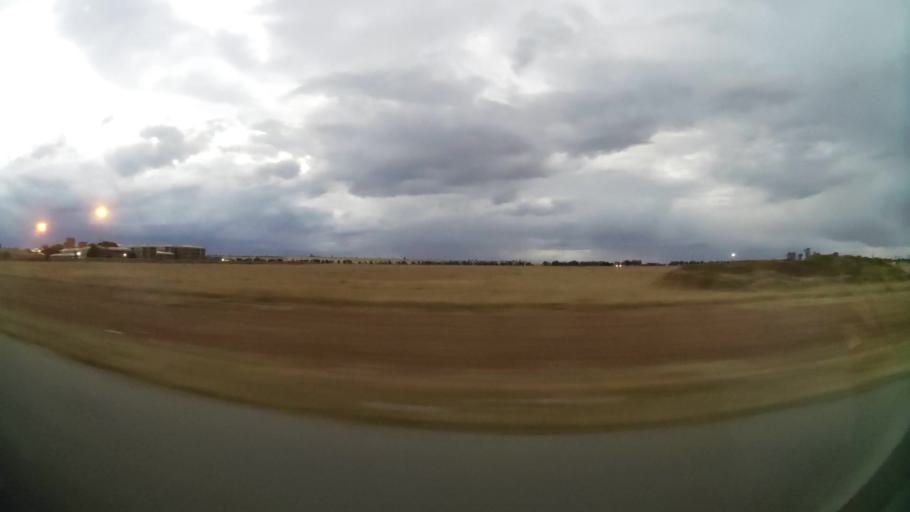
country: ZA
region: Orange Free State
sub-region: Lejweleputswa District Municipality
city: Welkom
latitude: -27.9512
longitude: 26.7928
